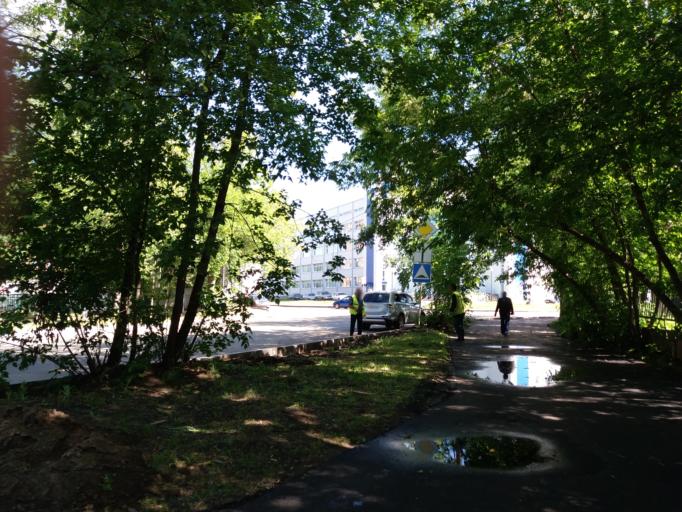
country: RU
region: Jaroslavl
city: Yaroslavl
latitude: 57.6404
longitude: 39.8530
